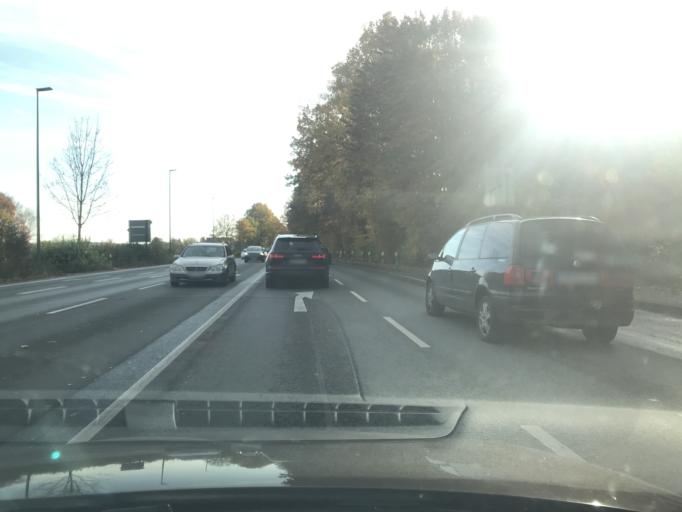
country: DE
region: North Rhine-Westphalia
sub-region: Regierungsbezirk Arnsberg
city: Hamm
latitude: 51.6539
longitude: 7.8388
